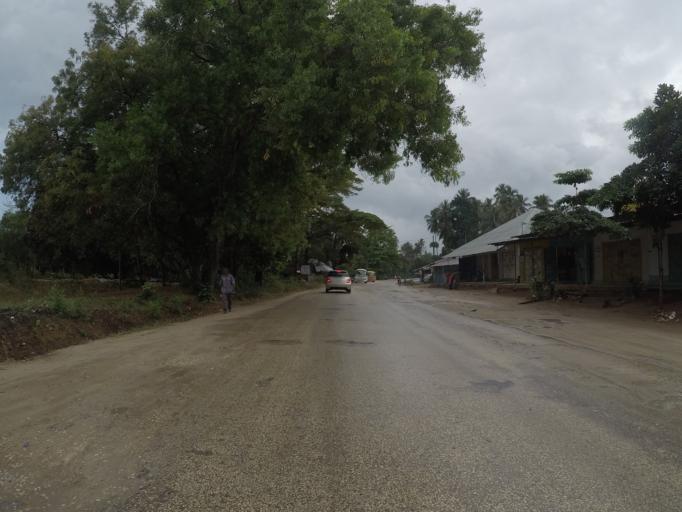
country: TZ
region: Zanzibar Urban/West
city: Zanzibar
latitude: -6.0937
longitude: 39.2191
